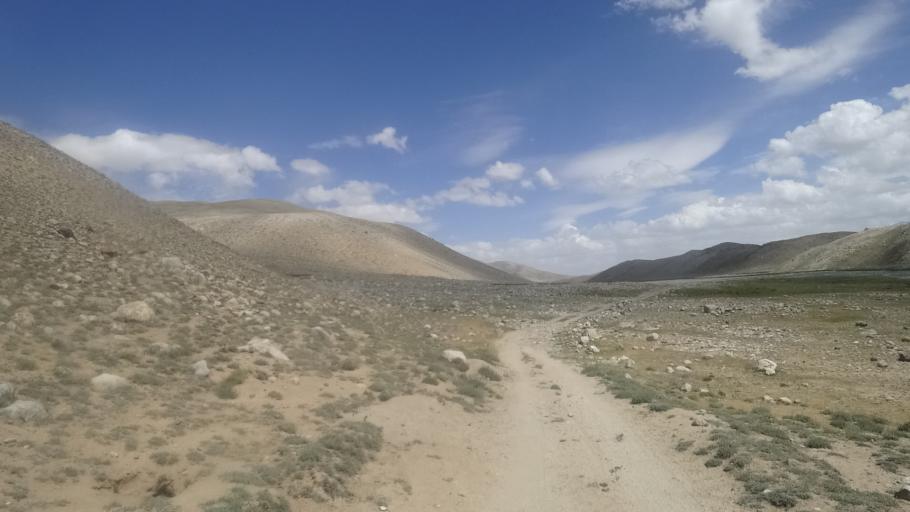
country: TJ
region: Gorno-Badakhshan
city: Murghob
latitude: 37.4751
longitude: 73.4540
